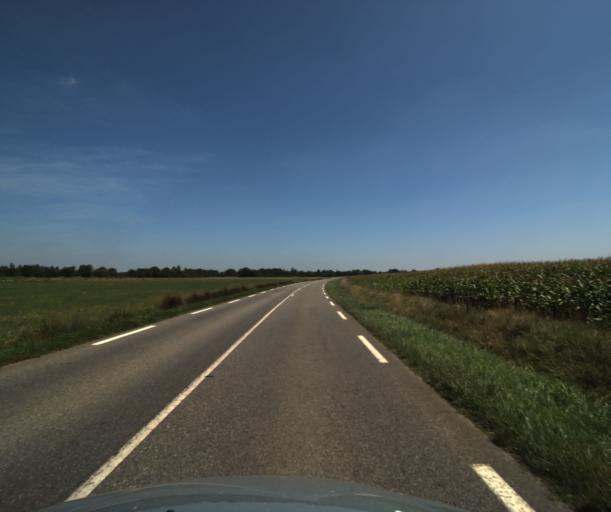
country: FR
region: Midi-Pyrenees
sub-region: Departement de la Haute-Garonne
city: Fonsorbes
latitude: 43.5104
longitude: 1.2258
